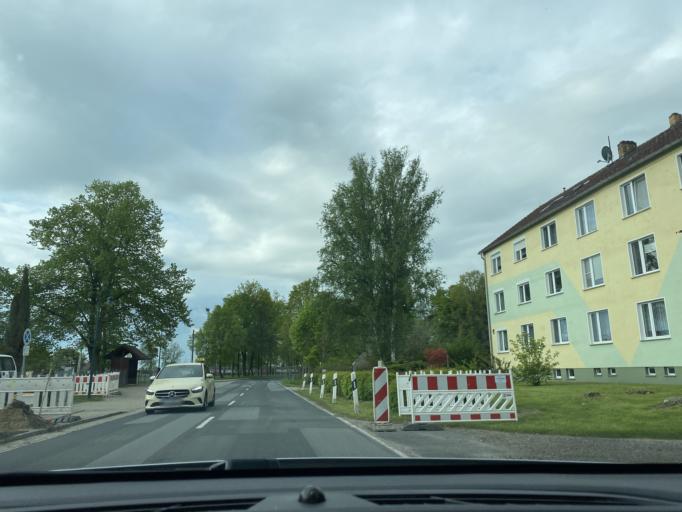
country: DE
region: Saxony
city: Horka
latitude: 51.2990
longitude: 14.8963
